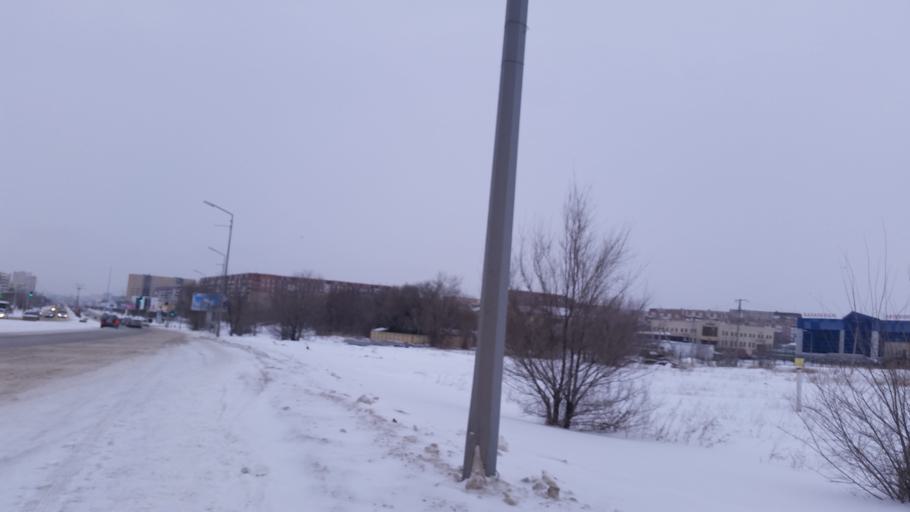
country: KZ
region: Qaraghandy
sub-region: Qaraghandy Qalasy
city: Karagandy
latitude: 49.7761
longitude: 73.1553
